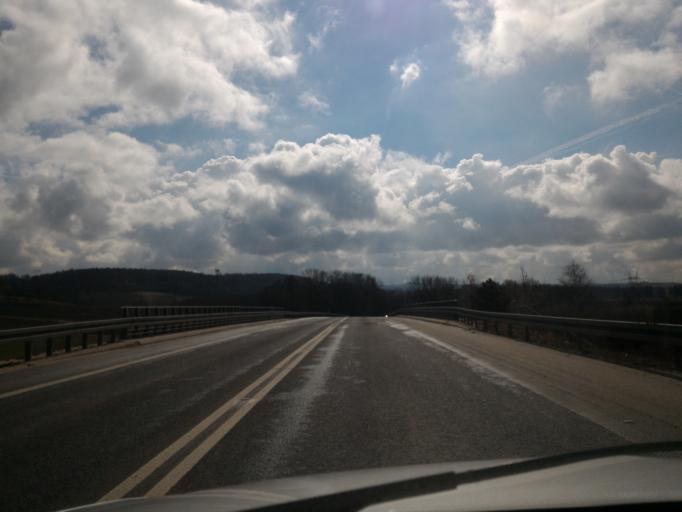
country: DE
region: Saxony
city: Ostritz
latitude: 51.0581
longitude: 14.9807
